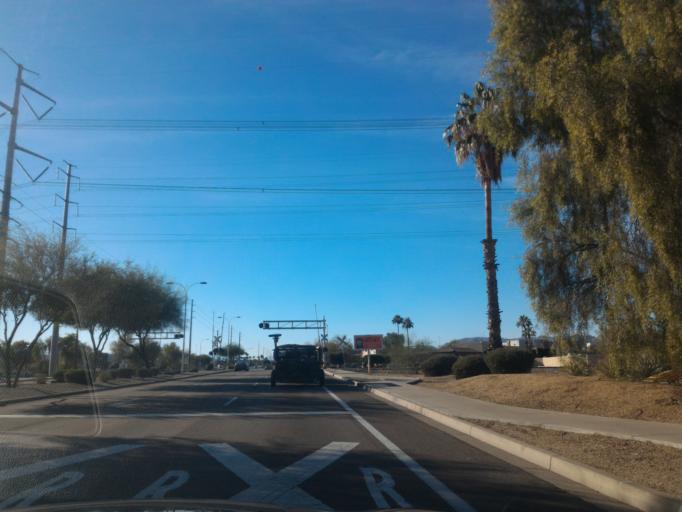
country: US
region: Arizona
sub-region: Maricopa County
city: Guadalupe
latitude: 33.3054
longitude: -111.9593
